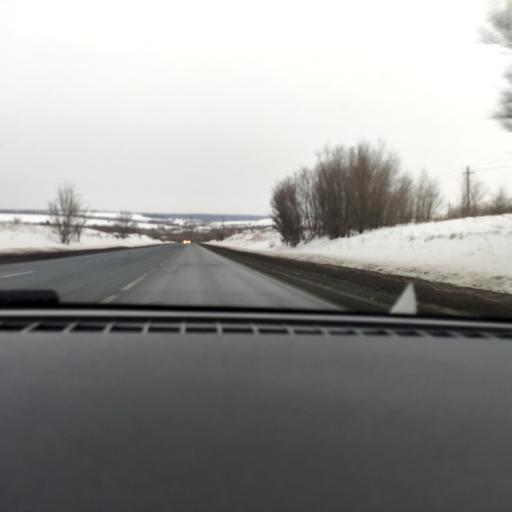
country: RU
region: Samara
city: Smyshlyayevka
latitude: 53.2734
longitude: 50.4657
